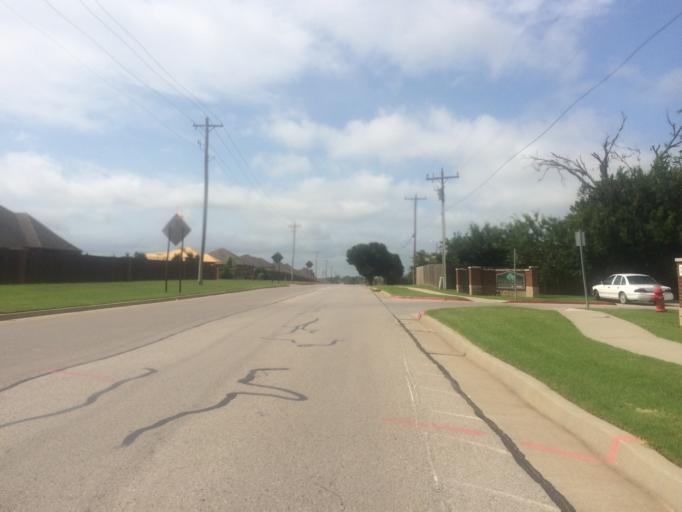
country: US
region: Oklahoma
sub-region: Cleveland County
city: Noble
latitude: 35.1726
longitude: -97.4236
